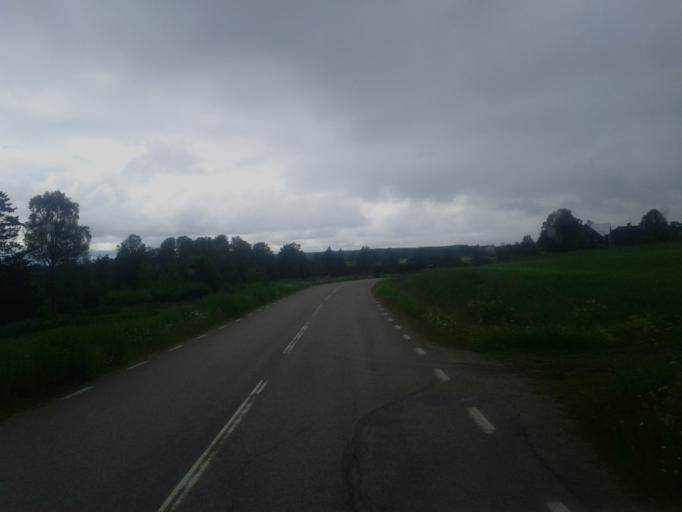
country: SE
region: Gaevleborg
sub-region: Nordanstigs Kommun
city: Bergsjoe
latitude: 61.9794
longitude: 17.2731
